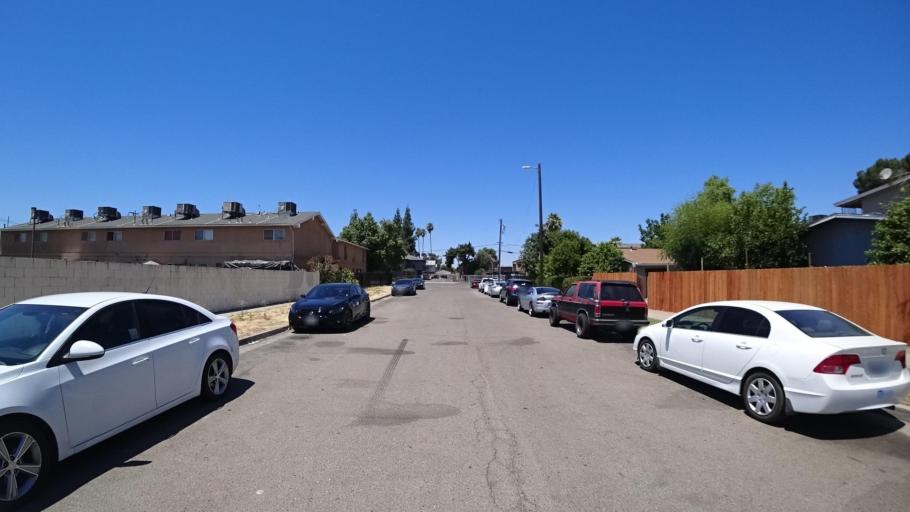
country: US
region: California
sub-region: Fresno County
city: Fresno
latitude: 36.7805
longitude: -119.7445
